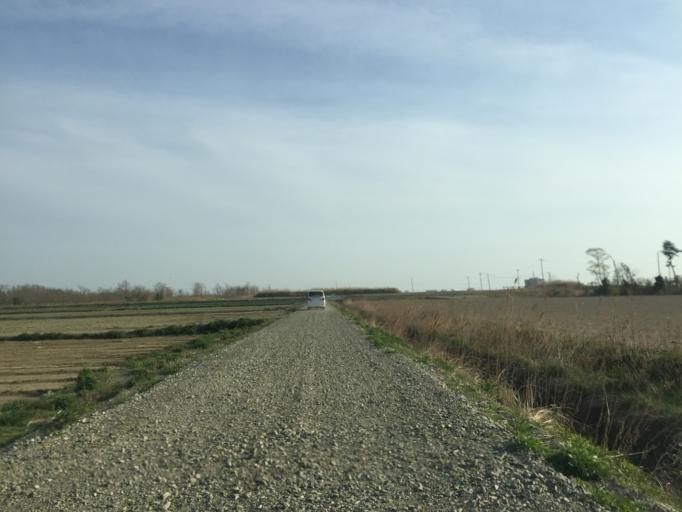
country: JP
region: Miyagi
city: Watari
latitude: 38.0265
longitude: 140.9122
